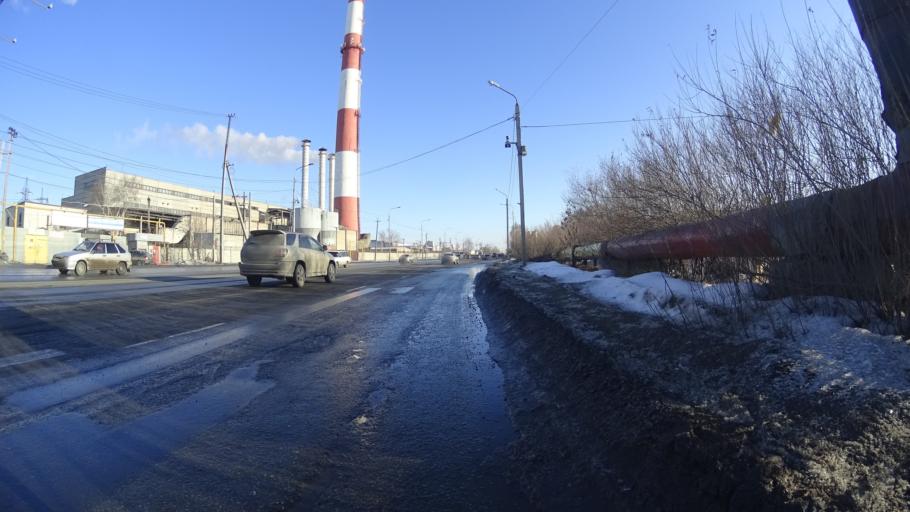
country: RU
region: Chelyabinsk
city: Roshchino
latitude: 55.2078
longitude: 61.3181
